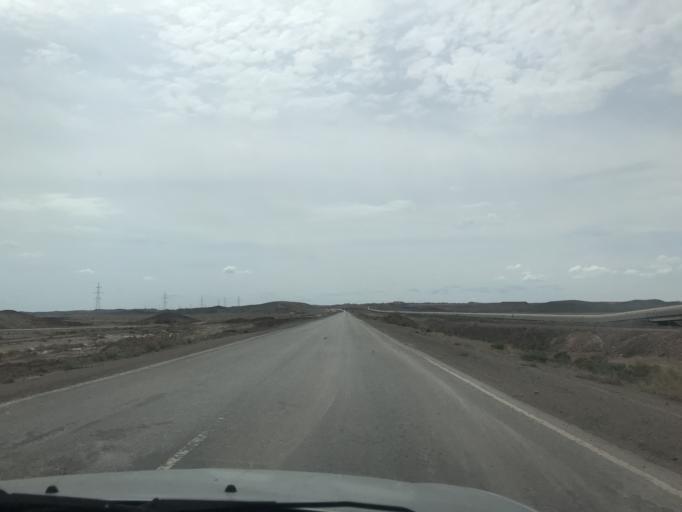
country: KZ
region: Zhambyl
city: Mynaral
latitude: 45.3825
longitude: 73.6515
